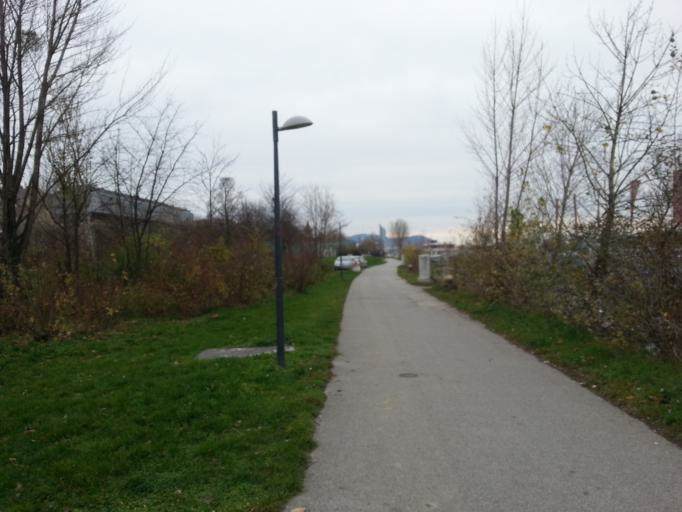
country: AT
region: Vienna
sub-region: Wien Stadt
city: Vienna
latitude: 48.2183
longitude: 16.4163
